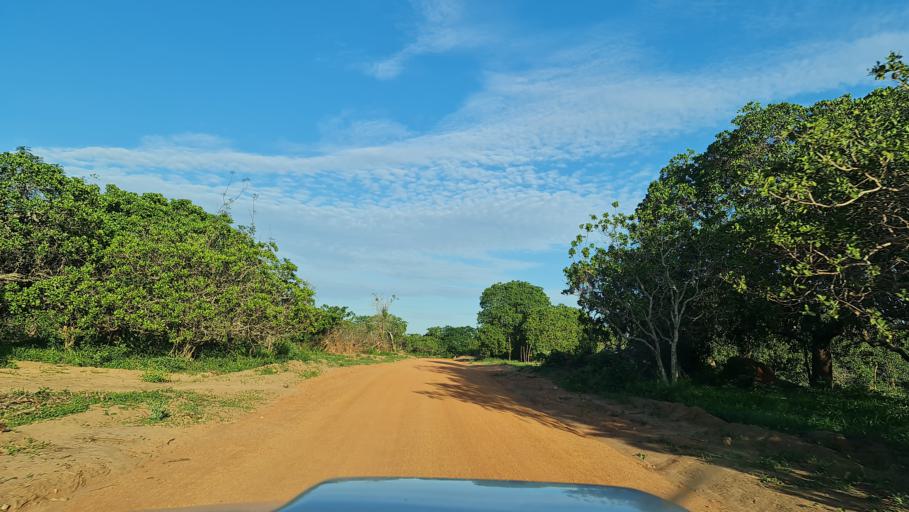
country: MZ
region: Nampula
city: Nacala
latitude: -14.6733
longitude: 40.2863
